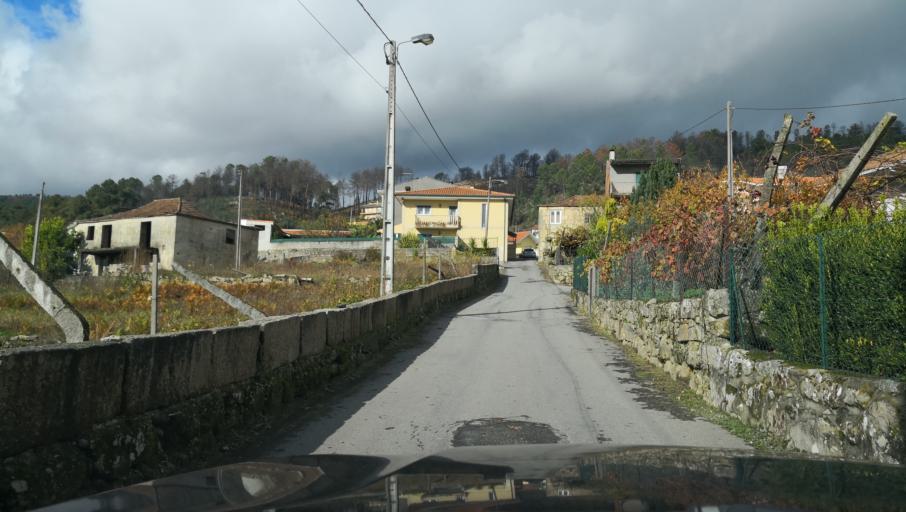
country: PT
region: Vila Real
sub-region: Vila Real
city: Vila Real
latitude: 41.3209
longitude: -7.7591
